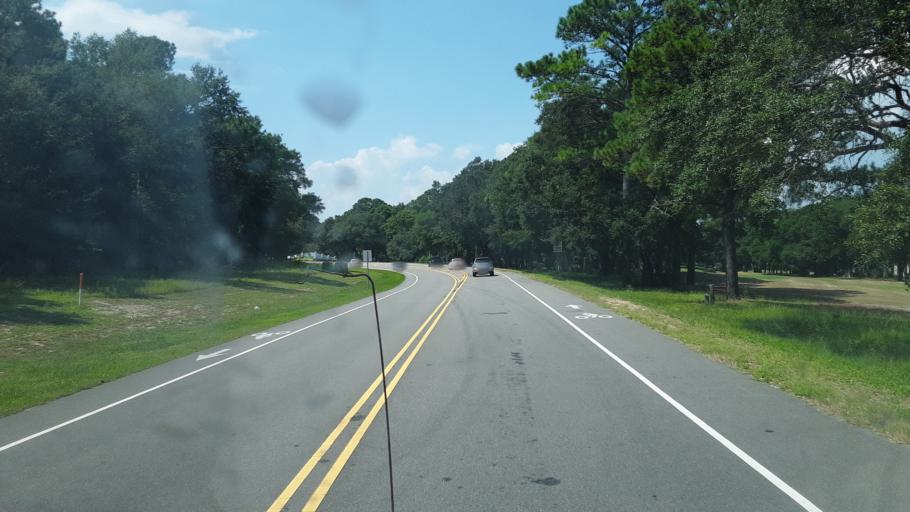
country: US
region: North Carolina
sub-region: Brunswick County
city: Sunset Beach
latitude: 33.8911
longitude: -78.5080
